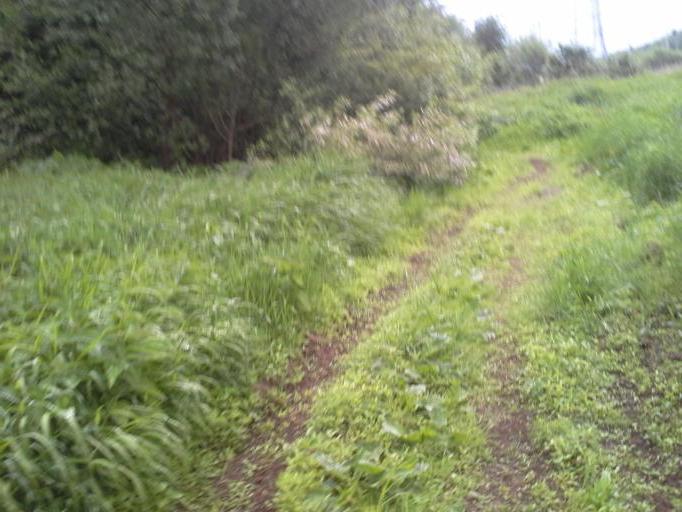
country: RU
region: Moskovskaya
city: Lesnoy Gorodok
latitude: 55.6358
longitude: 37.2440
